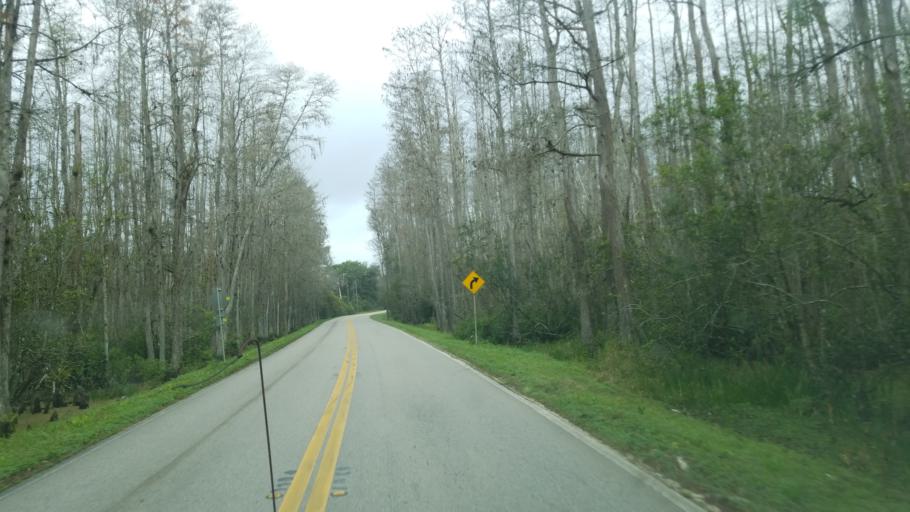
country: US
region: Florida
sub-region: Lake County
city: Four Corners
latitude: 28.2591
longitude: -81.7122
